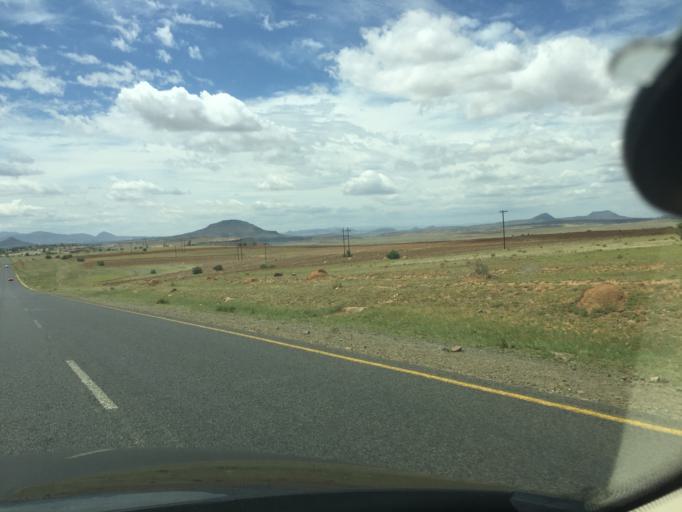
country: LS
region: Mohale's Hoek District
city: Mohale's Hoek
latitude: -30.0010
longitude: 27.3431
